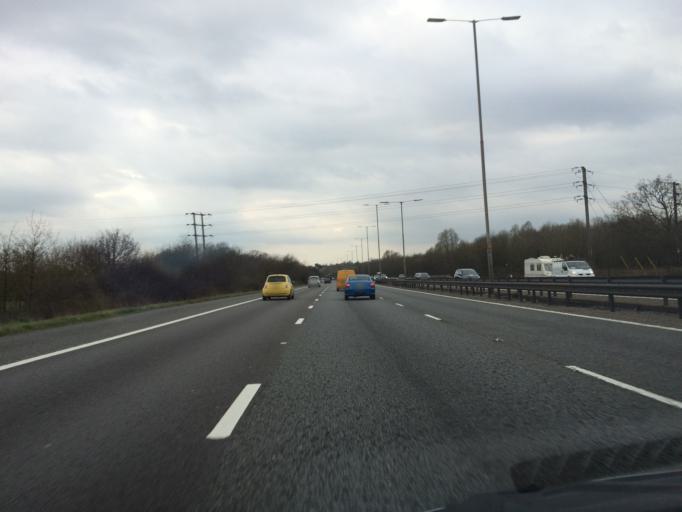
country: GB
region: England
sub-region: Wokingham
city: Lower Earley
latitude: 51.4199
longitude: -0.9175
